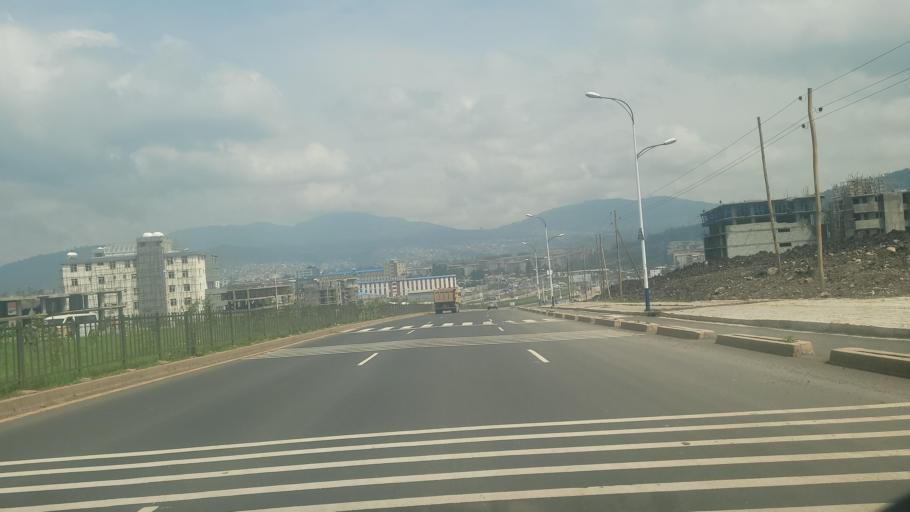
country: ET
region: Adis Abeba
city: Addis Ababa
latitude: 8.9513
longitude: 38.7015
